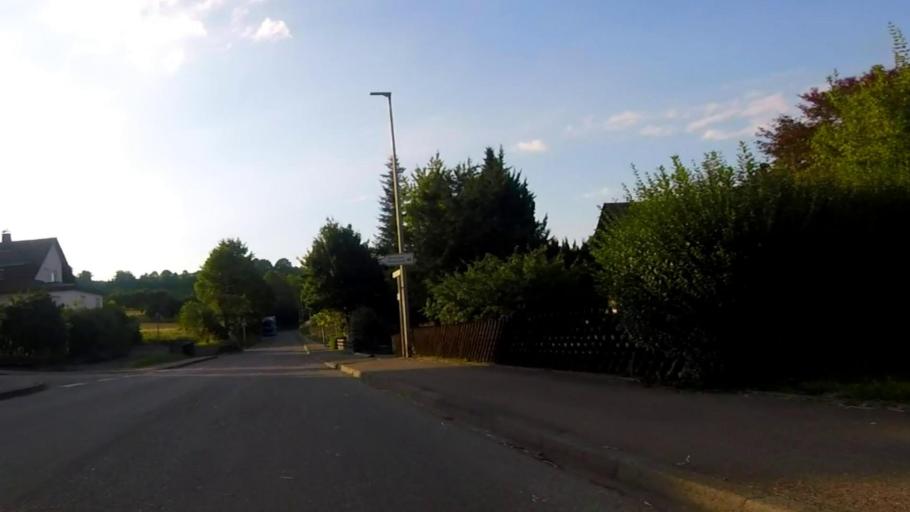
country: DE
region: Baden-Wuerttemberg
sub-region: Regierungsbezirk Stuttgart
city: Oppenweiler
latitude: 48.9871
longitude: 9.4587
